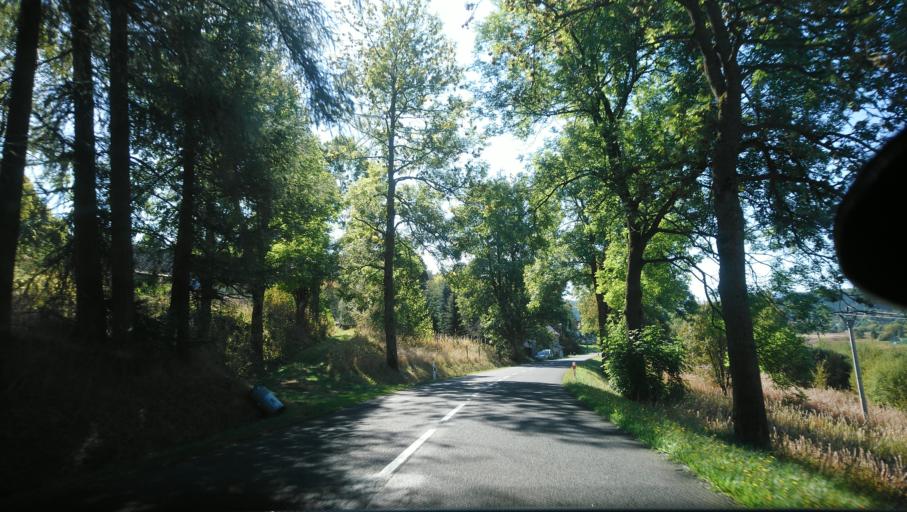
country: CZ
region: Ustecky
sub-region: Okres Chomutov
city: Kovarska
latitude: 50.4475
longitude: 13.0218
